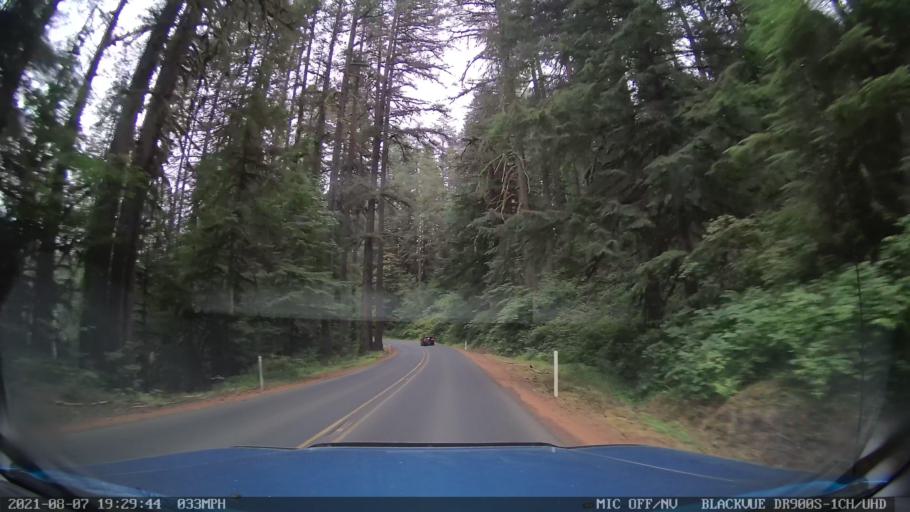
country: US
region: Oregon
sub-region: Linn County
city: Lyons
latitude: 44.8831
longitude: -122.6258
